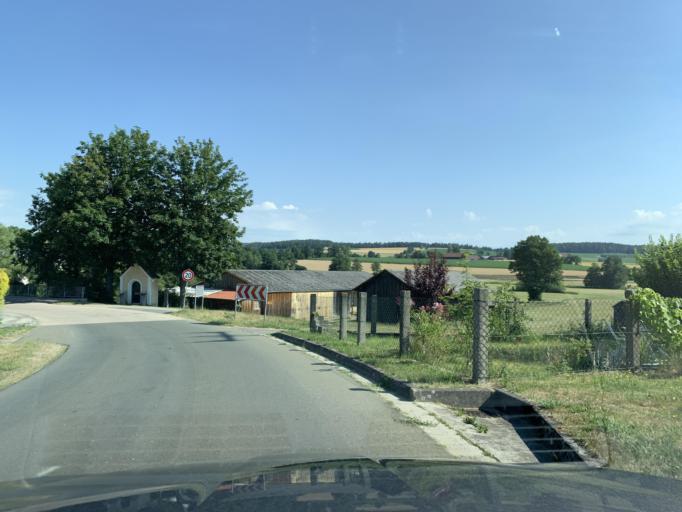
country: DE
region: Bavaria
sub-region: Upper Palatinate
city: Altendorf
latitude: 49.3967
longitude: 12.3111
